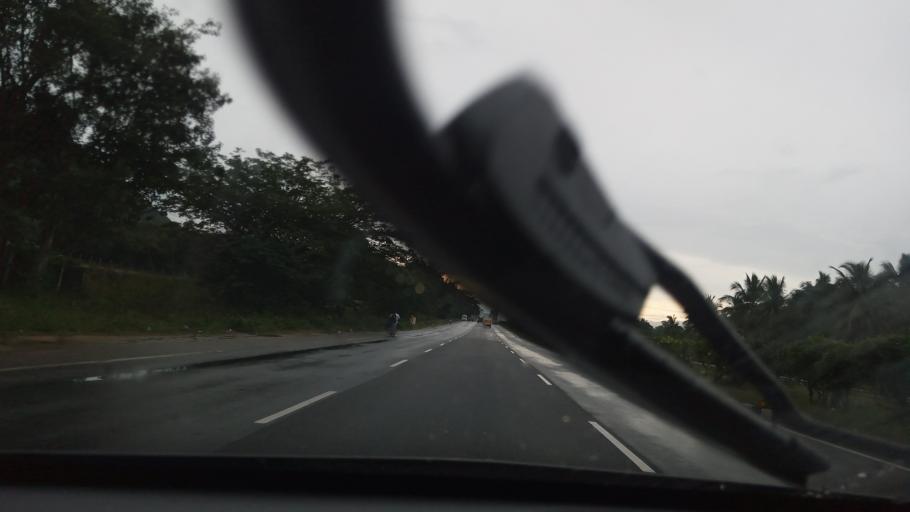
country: IN
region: Tamil Nadu
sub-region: Vellore
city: Ambur
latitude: 12.8484
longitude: 78.8077
